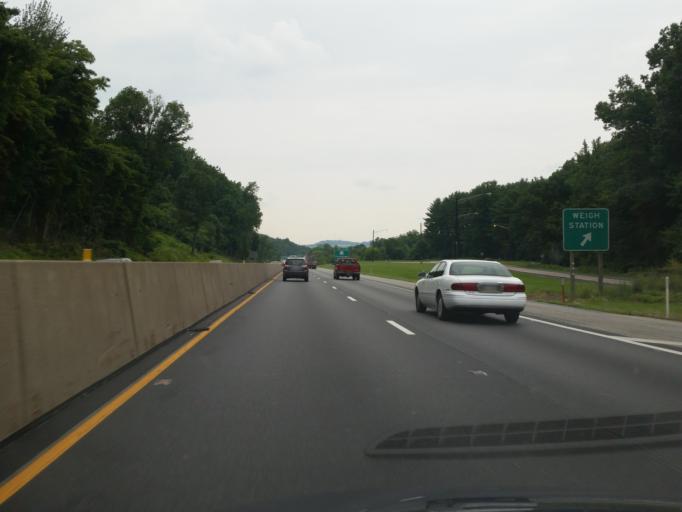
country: US
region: Pennsylvania
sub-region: York County
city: Valley Green
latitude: 40.1380
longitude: -76.8049
